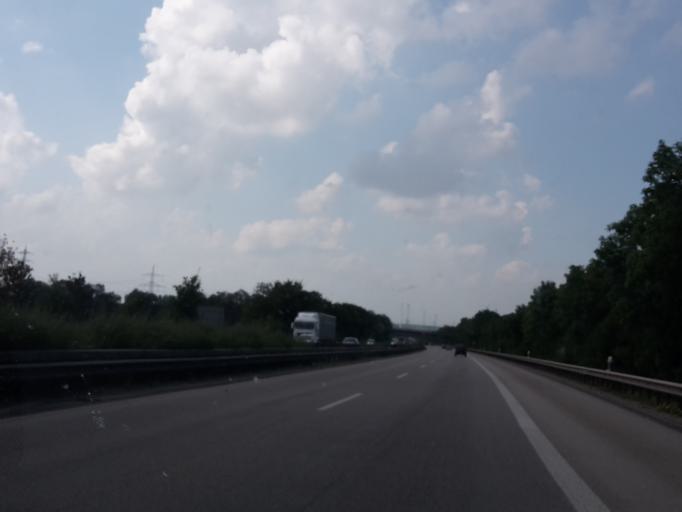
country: DE
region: Rheinland-Pfalz
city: Lonsheim
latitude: 49.7918
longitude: 8.0867
